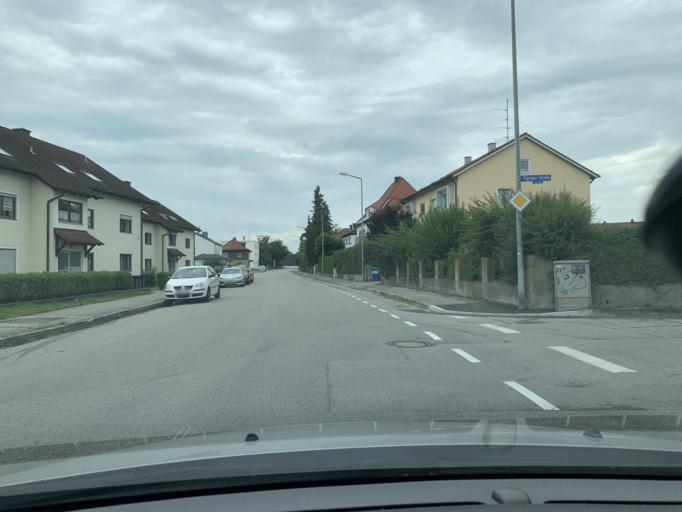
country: DE
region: Bavaria
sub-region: Upper Bavaria
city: Muehldorf
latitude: 48.2468
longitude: 12.5330
